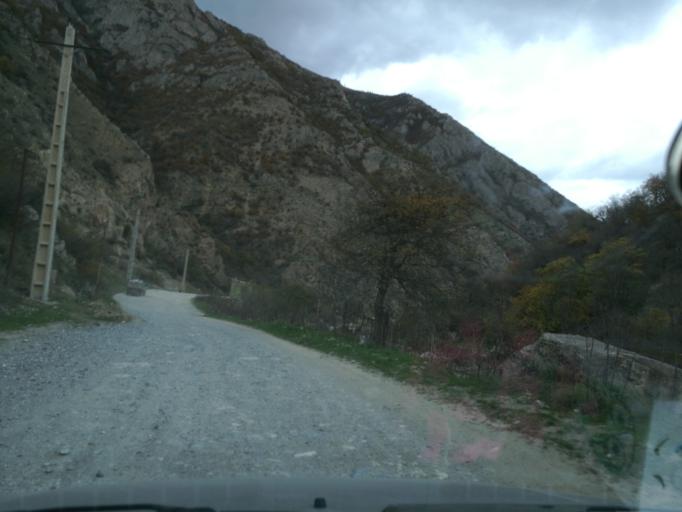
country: IR
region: Mazandaran
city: `Abbasabad
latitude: 36.4454
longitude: 51.0629
